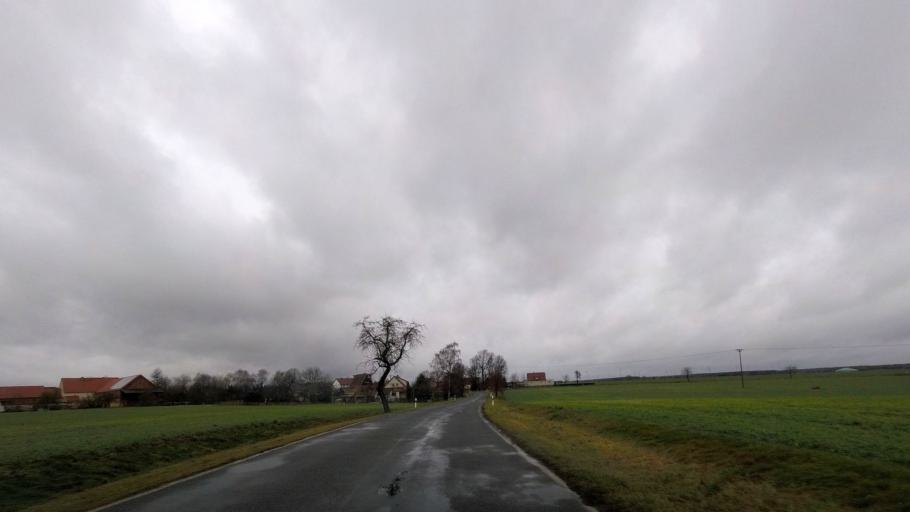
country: DE
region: Brandenburg
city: Niedergorsdorf
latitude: 51.9713
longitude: 12.9703
